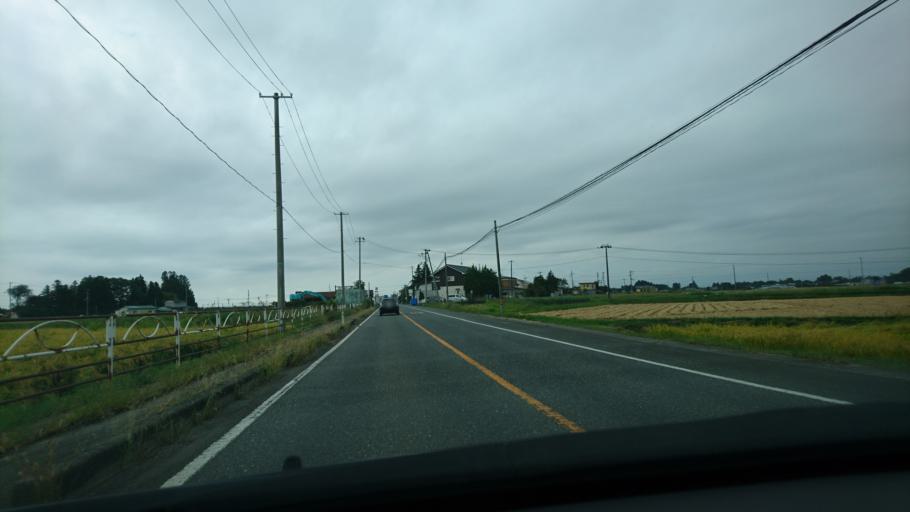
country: JP
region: Iwate
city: Ichinoseki
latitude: 38.7590
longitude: 141.0757
